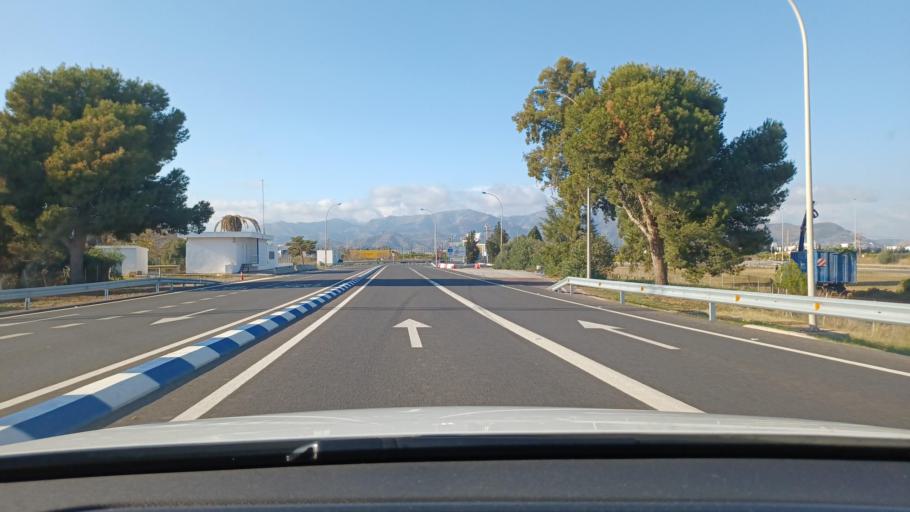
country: ES
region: Valencia
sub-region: Provincia de Castello
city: Moncofar
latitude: 39.8122
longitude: -0.1594
